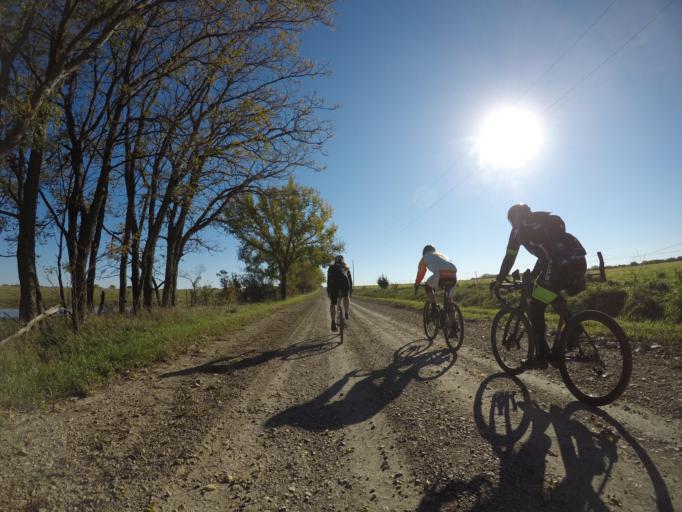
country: US
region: Kansas
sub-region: Morris County
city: Council Grove
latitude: 38.8259
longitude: -96.4548
